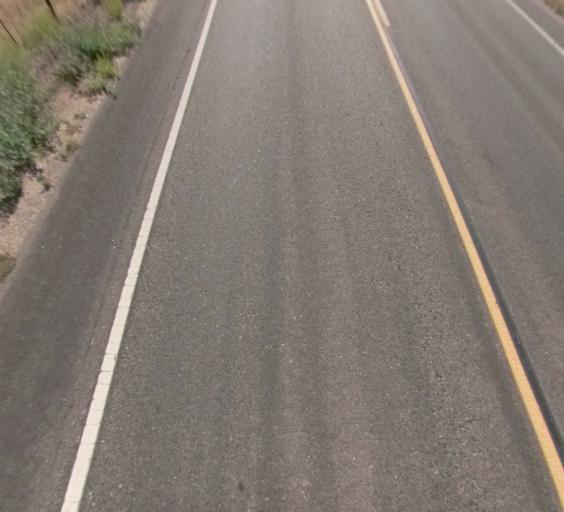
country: US
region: California
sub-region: Madera County
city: Bonadelle Ranchos-Madera Ranchos
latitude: 36.9666
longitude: -119.9256
